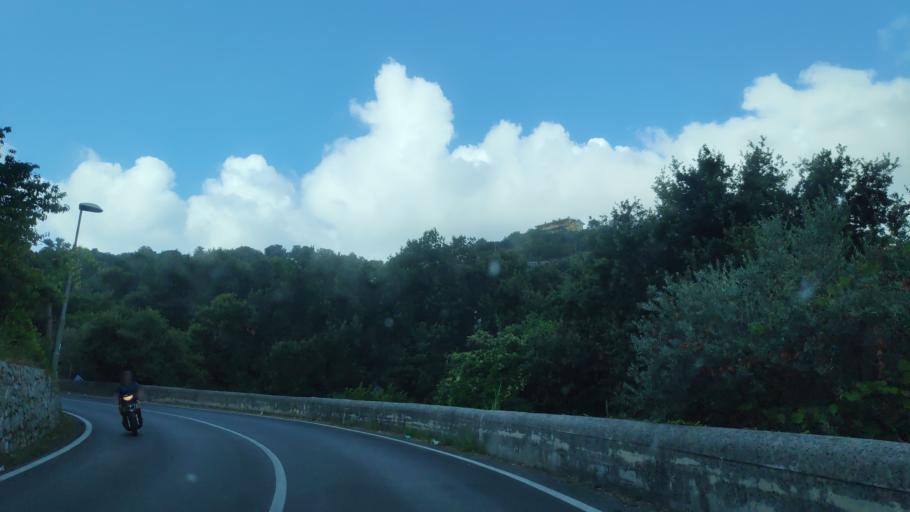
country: IT
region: Campania
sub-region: Provincia di Napoli
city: Piano di Sorrento
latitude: 40.6225
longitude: 14.4238
